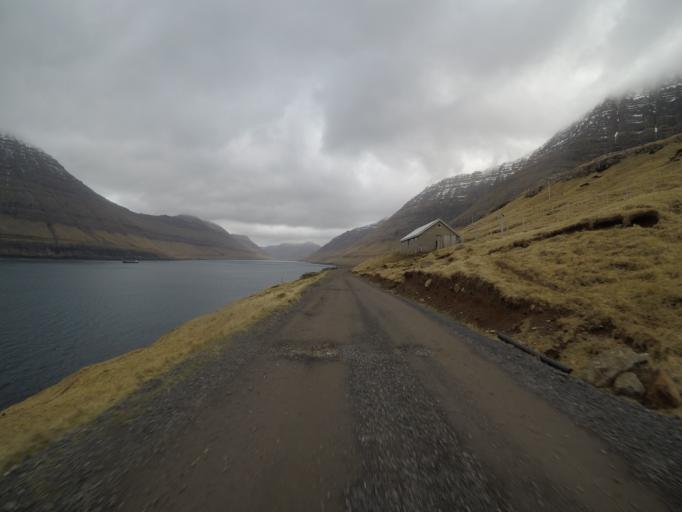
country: FO
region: Nordoyar
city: Klaksvik
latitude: 62.3475
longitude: -6.5808
